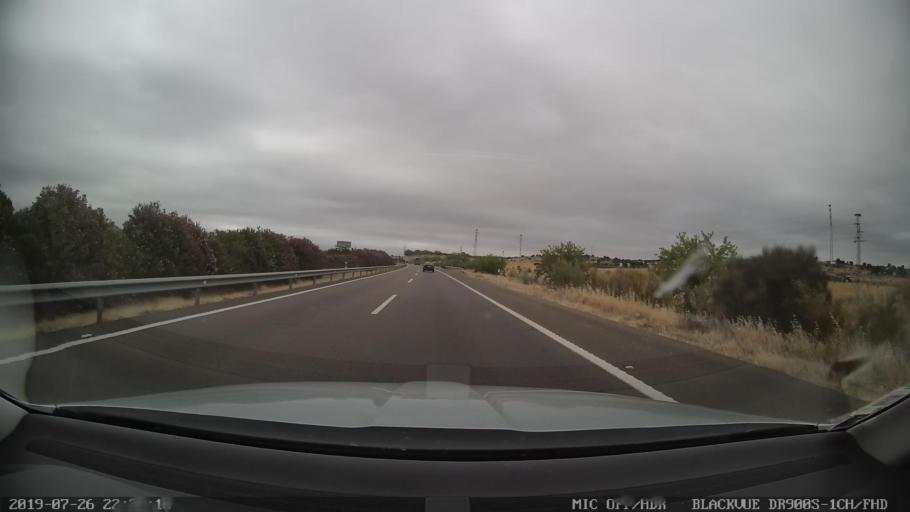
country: ES
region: Extremadura
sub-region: Provincia de Badajoz
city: Badajoz
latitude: 38.8792
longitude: -6.8845
